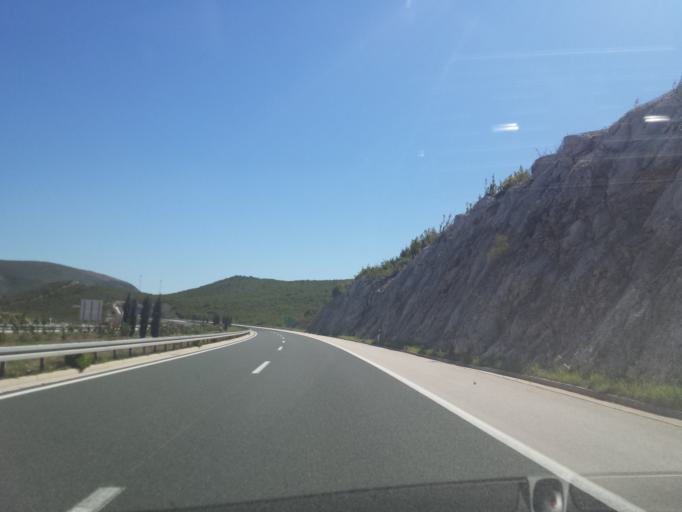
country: HR
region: Splitsko-Dalmatinska
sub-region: Grad Omis
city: Omis
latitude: 43.4793
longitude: 16.8103
